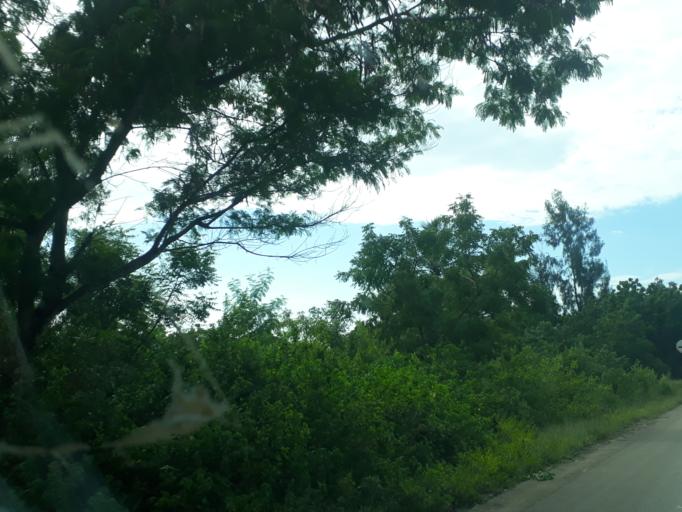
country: TZ
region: Zanzibar North
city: Kijini
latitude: -5.8426
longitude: 39.2839
